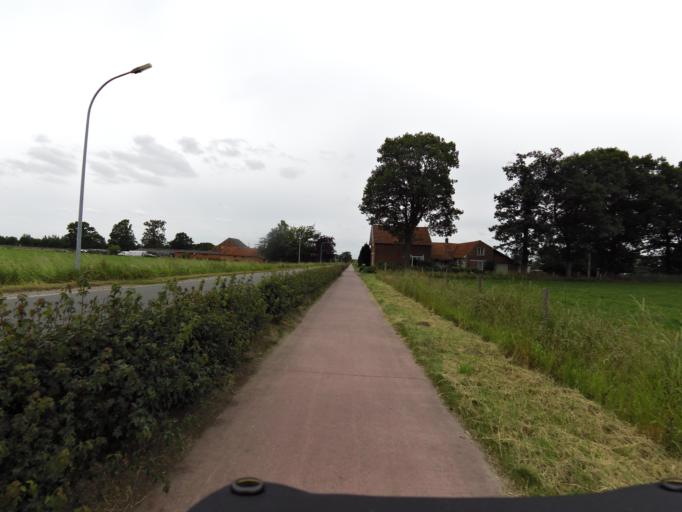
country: NL
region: North Brabant
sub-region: Gemeente Goirle
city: Goirle
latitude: 51.4404
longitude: 5.0548
